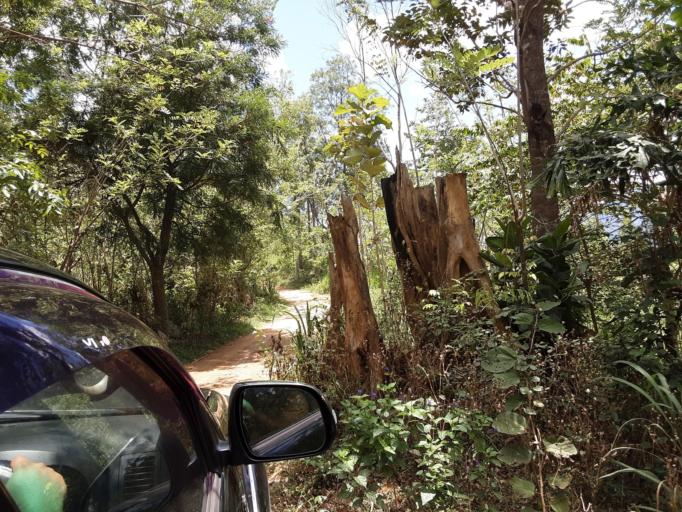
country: LK
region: Uva
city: Haputale
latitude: 6.8212
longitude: 81.1097
